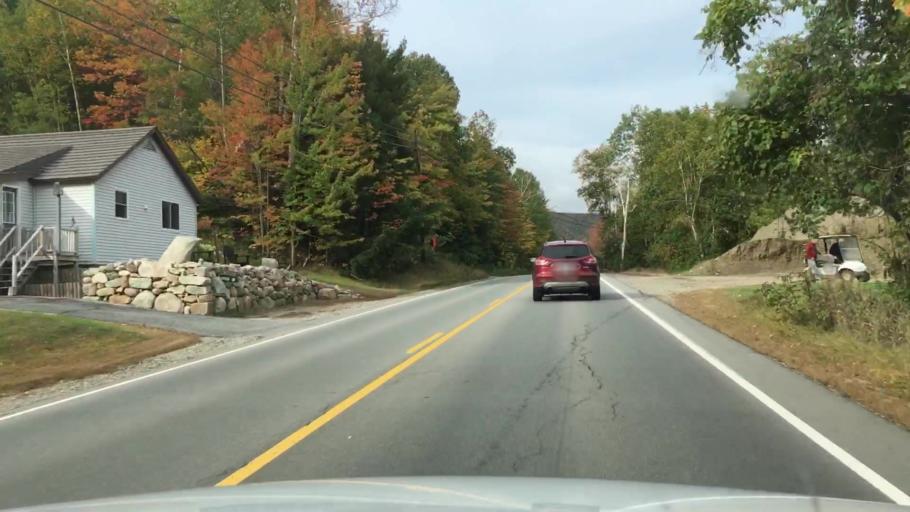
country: US
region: New Hampshire
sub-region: Coos County
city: Gorham
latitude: 44.3856
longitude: -71.1514
